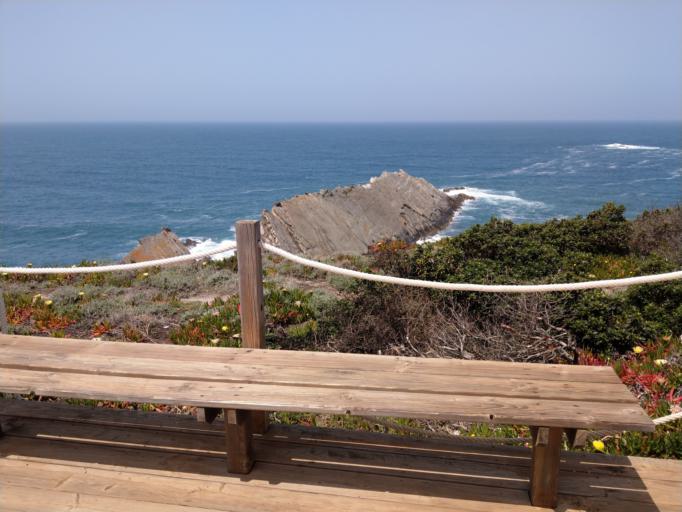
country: PT
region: Beja
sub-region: Odemira
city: Sao Teotonio
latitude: 37.5380
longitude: -8.7882
